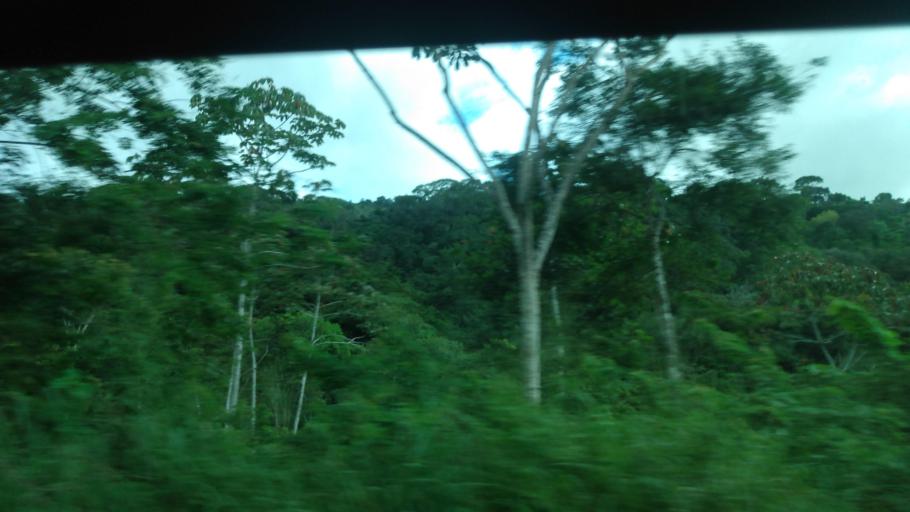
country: BR
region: Pernambuco
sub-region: Maraial
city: Maraial
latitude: -8.7834
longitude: -35.9088
